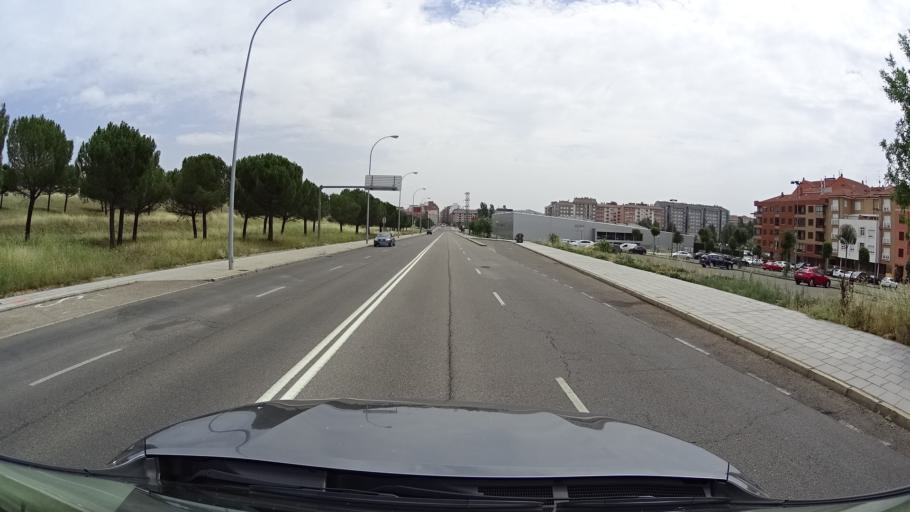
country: ES
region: Castille and Leon
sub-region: Provincia de Leon
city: Leon
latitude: 42.6123
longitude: -5.5839
